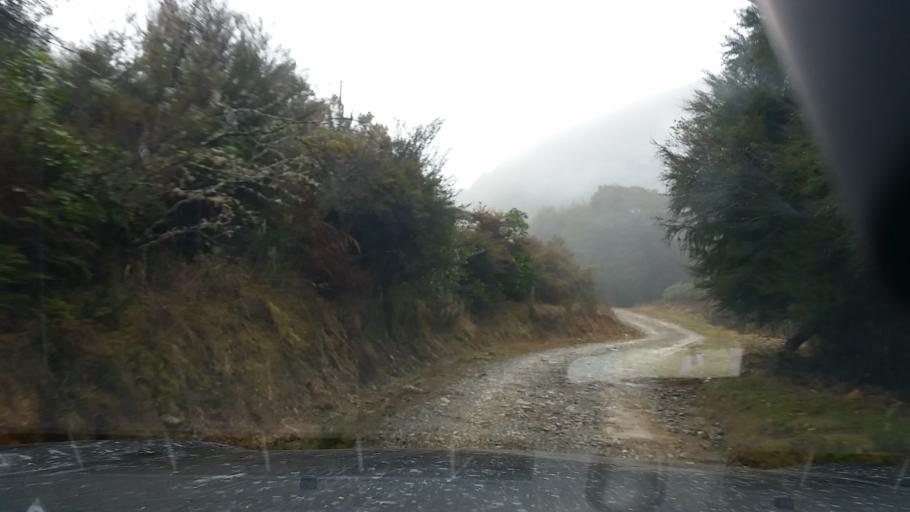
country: NZ
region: Nelson
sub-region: Nelson City
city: Nelson
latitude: -41.3762
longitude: 173.5950
